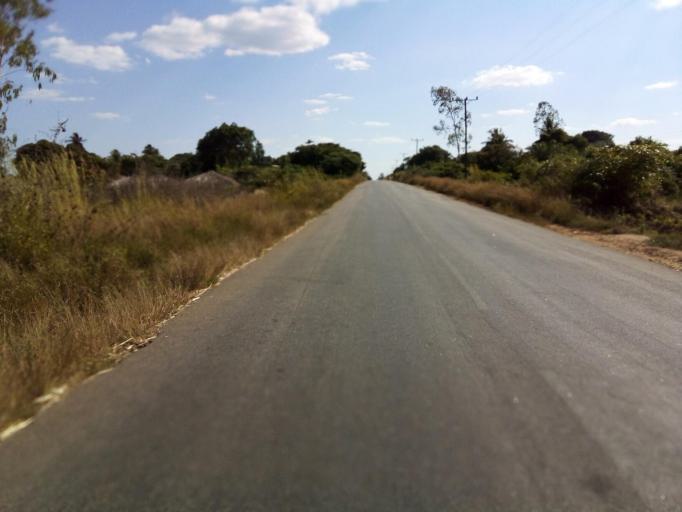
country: MZ
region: Zambezia
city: Quelimane
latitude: -17.5776
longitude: 36.6738
